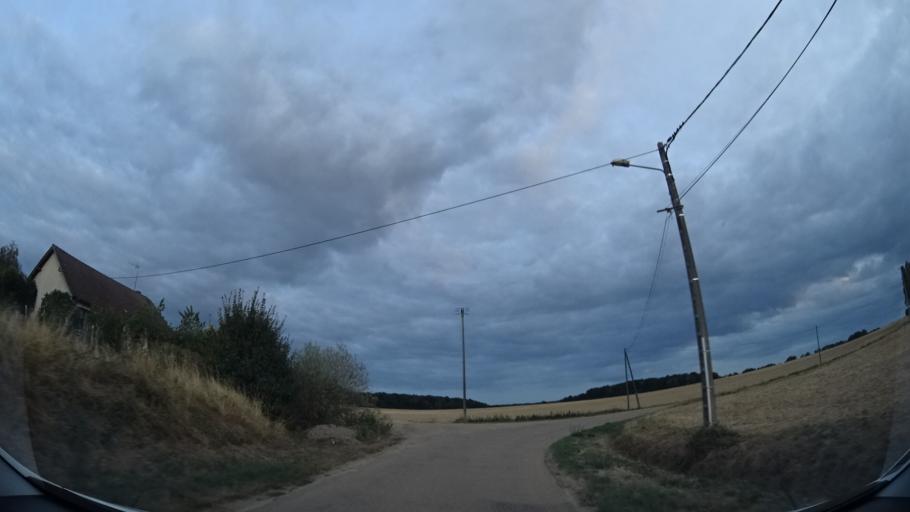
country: FR
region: Bourgogne
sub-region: Departement de l'Yonne
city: Cezy
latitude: 47.9334
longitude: 3.2761
